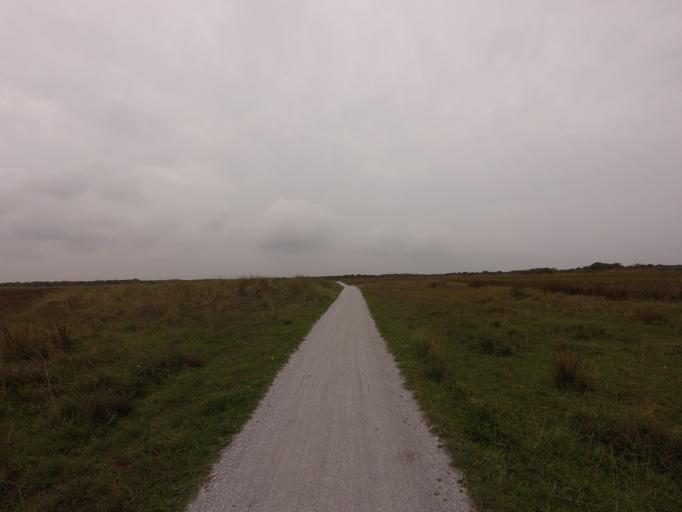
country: NL
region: Friesland
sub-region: Gemeente Schiermonnikoog
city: Schiermonnikoog
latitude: 53.4885
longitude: 6.2077
